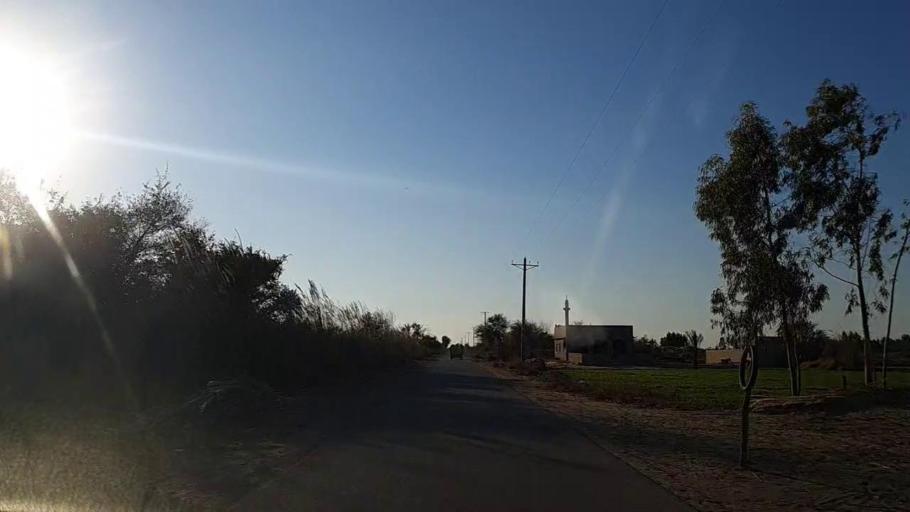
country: PK
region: Sindh
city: Khadro
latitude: 26.2790
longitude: 68.8886
